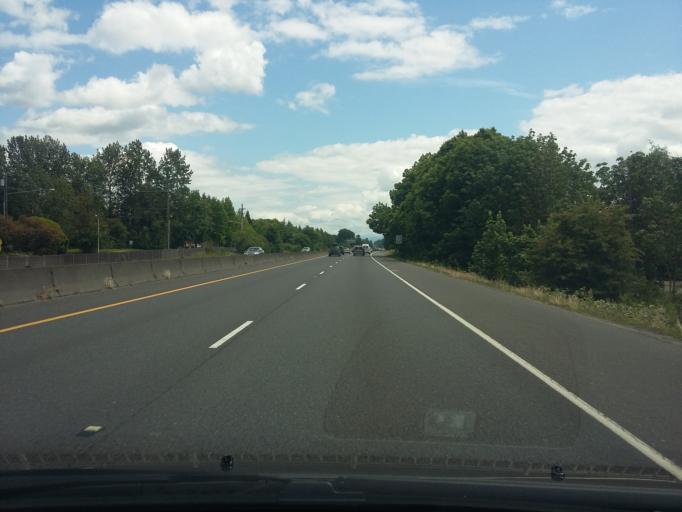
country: US
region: Washington
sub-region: Clark County
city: Mill Plain
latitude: 45.5976
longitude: -122.5260
